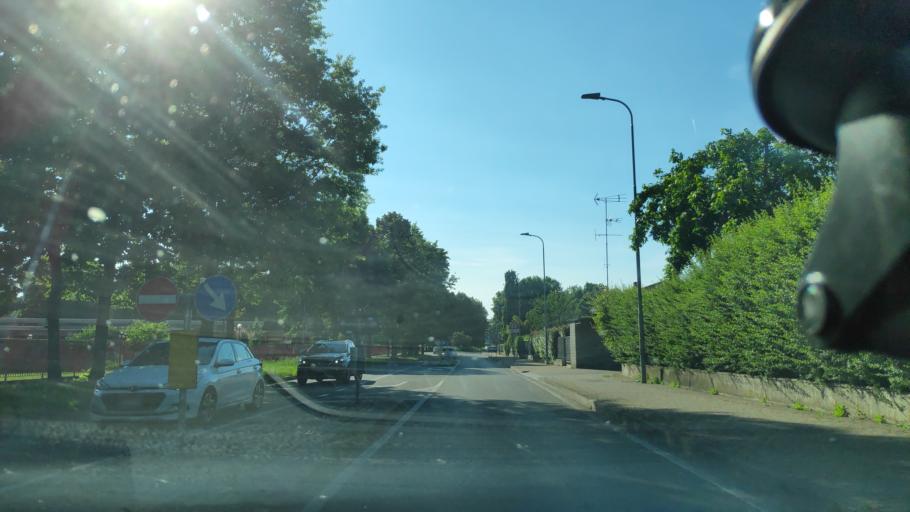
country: IT
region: Lombardy
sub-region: Citta metropolitana di Milano
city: Rozzano
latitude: 45.3781
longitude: 9.1466
